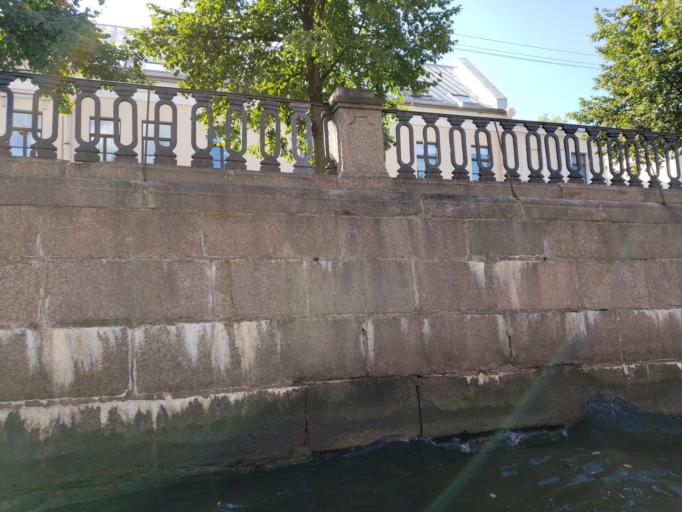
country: RU
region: St.-Petersburg
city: Admiralteisky
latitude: 59.9195
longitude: 30.2999
